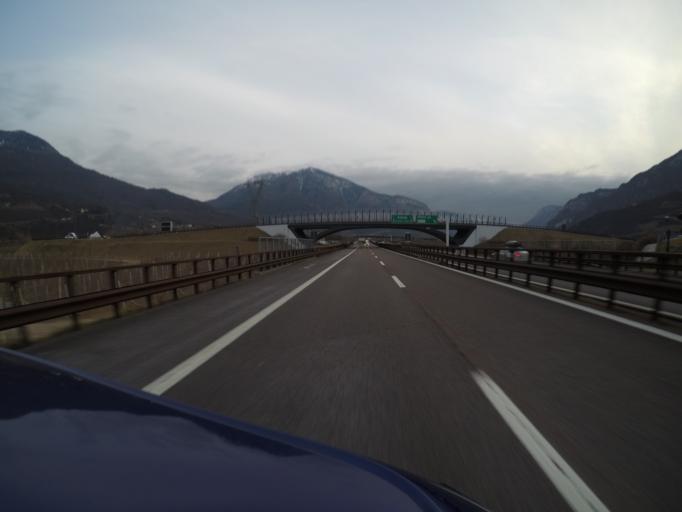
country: IT
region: Trentino-Alto Adige
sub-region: Provincia di Trento
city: Ravina
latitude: 46.0358
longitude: 11.1198
